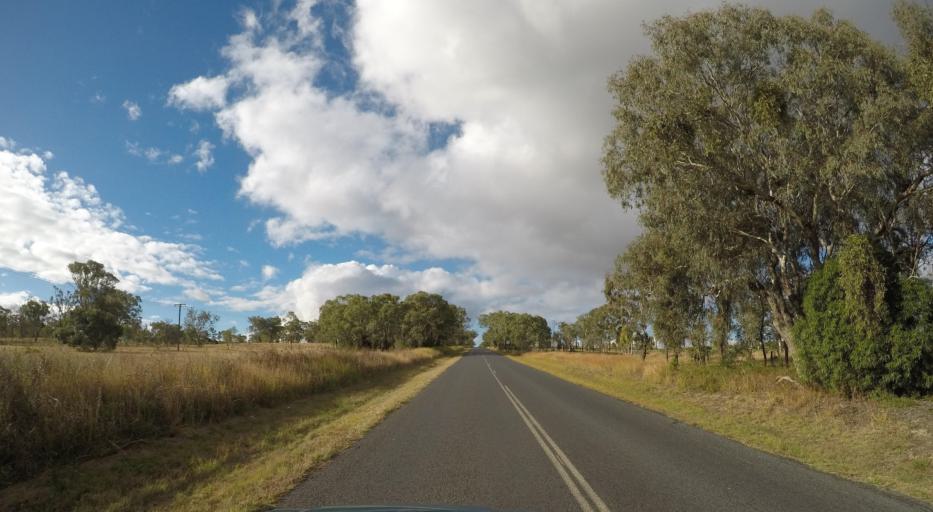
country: AU
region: Queensland
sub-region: Toowoomba
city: Westbrook
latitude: -27.7016
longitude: 151.6604
